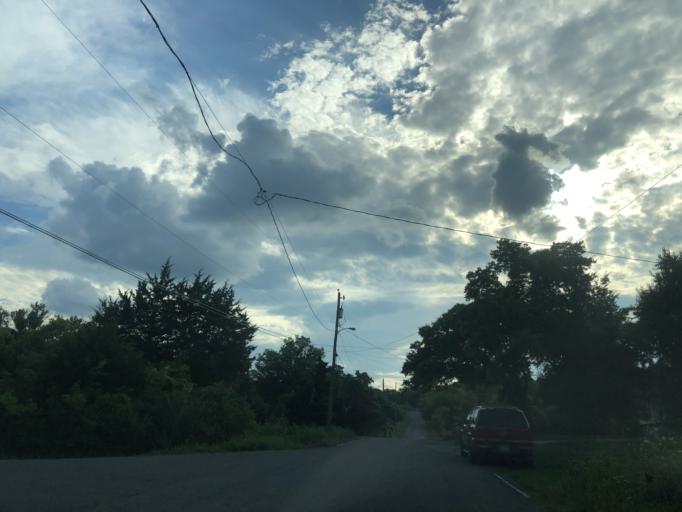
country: US
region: Tennessee
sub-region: Davidson County
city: Nashville
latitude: 36.2178
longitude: -86.7827
